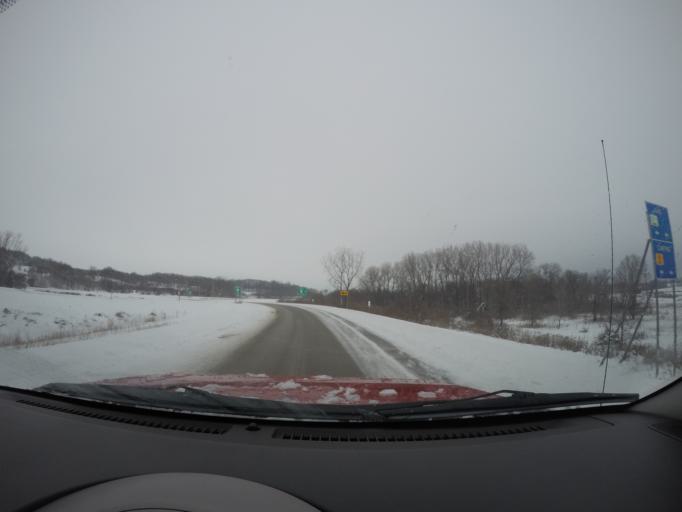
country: US
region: Minnesota
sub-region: Olmsted County
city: Rochester
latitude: 43.9525
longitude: -92.3567
